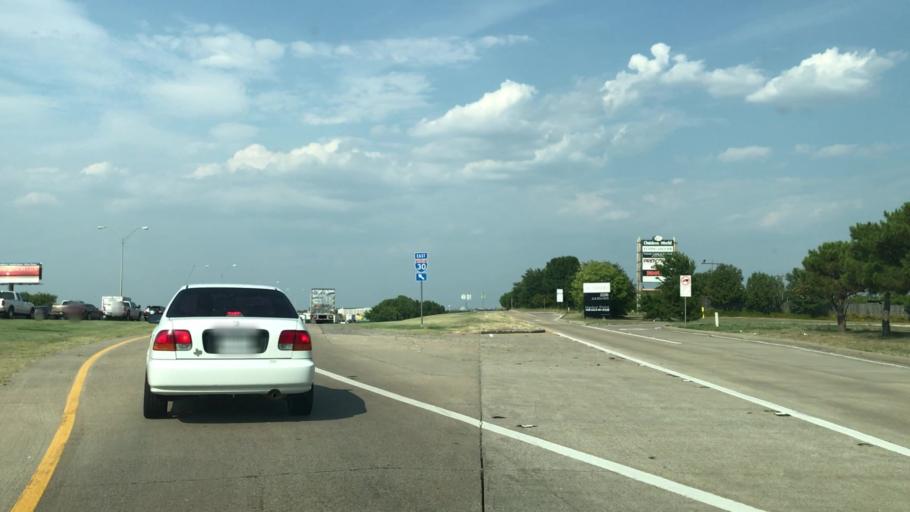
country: US
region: Texas
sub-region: Dallas County
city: Rowlett
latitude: 32.8652
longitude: -96.5422
